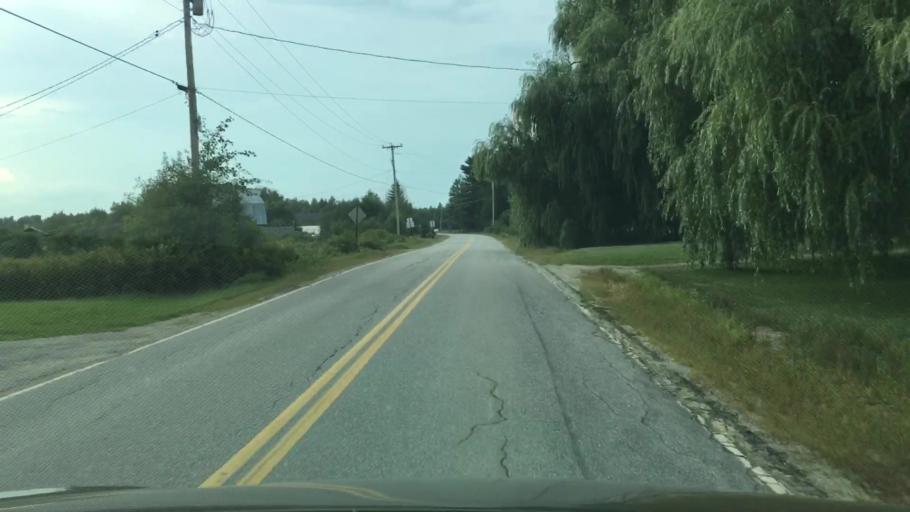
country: US
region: Maine
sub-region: Hancock County
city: Penobscot
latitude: 44.4694
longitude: -68.7413
